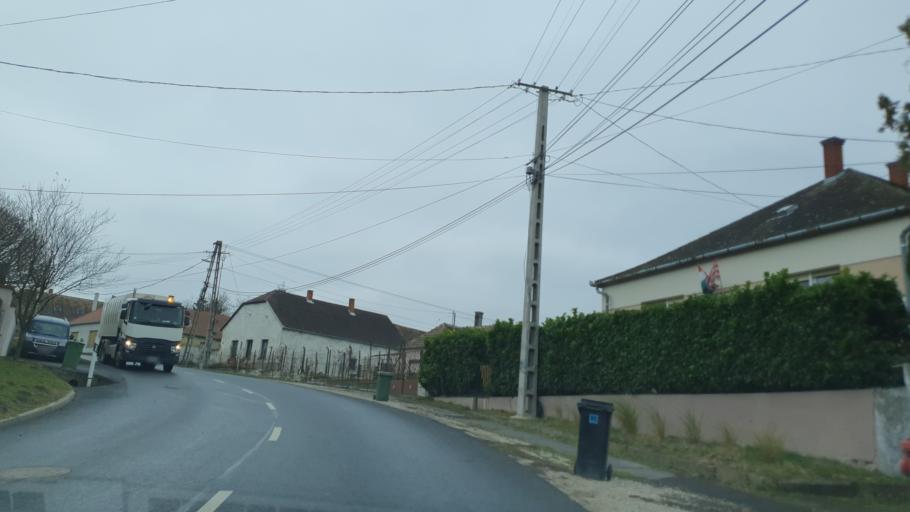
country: HU
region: Veszprem
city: Sumeg
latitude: 46.9330
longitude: 17.2437
